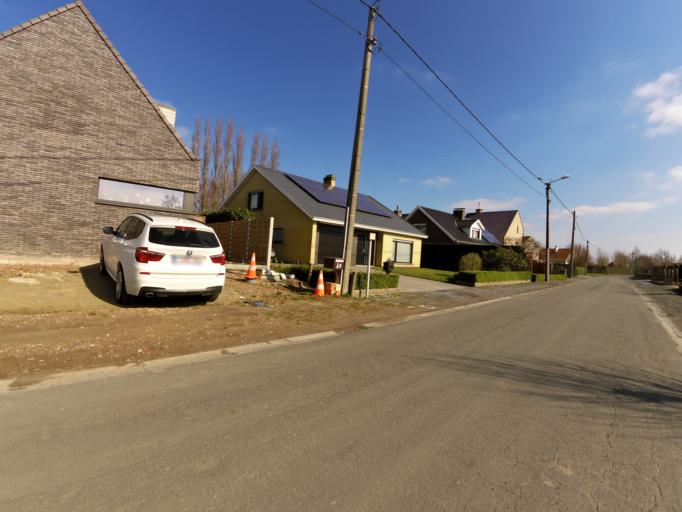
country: BE
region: Flanders
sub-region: Provincie West-Vlaanderen
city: Torhout
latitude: 51.0518
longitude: 3.1145
